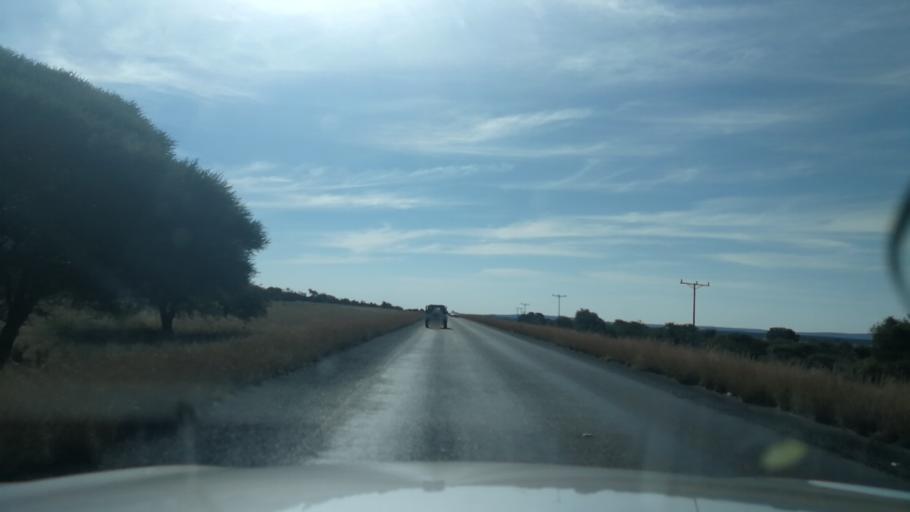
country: BW
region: South East
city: Janeng
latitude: -25.3291
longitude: 25.6182
